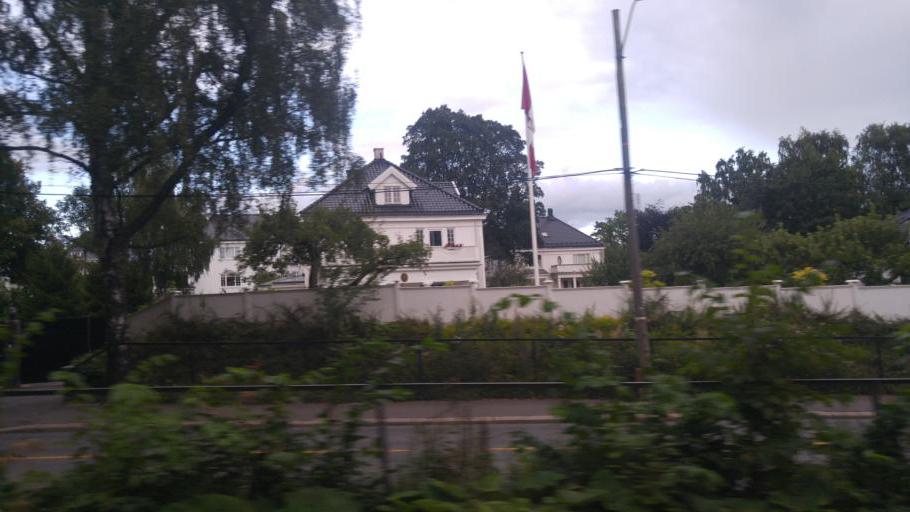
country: NO
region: Oslo
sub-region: Oslo
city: Sjolyststranda
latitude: 59.9377
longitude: 10.7059
